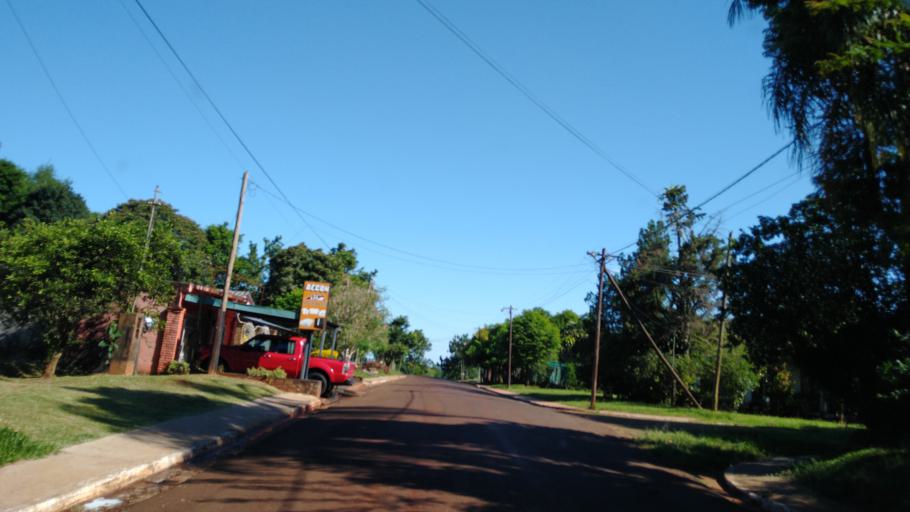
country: AR
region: Misiones
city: Garupa
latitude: -27.4836
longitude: -55.8315
